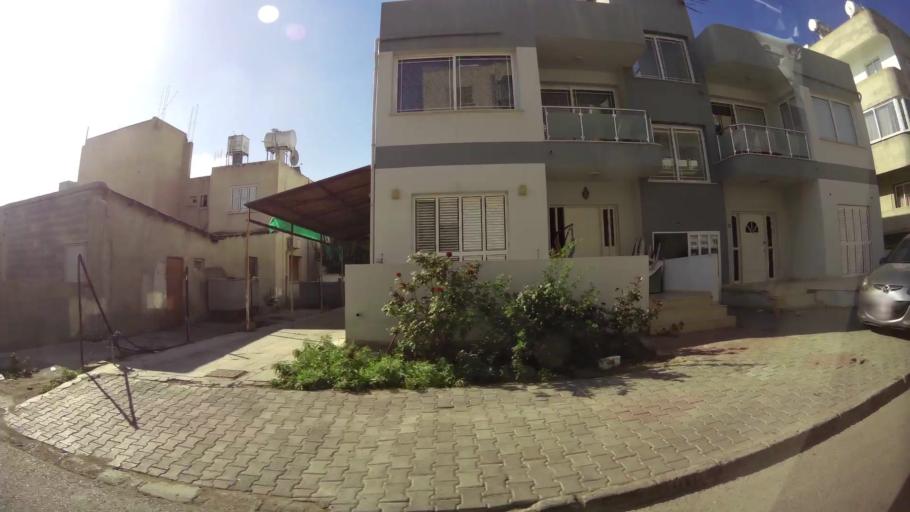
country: CY
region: Lefkosia
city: Nicosia
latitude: 35.2109
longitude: 33.3154
